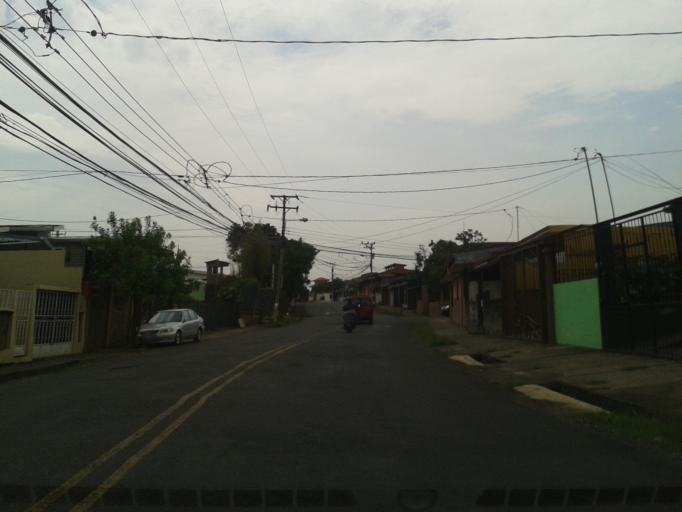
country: CR
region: Heredia
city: San Pablo
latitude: 9.9799
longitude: -84.0987
